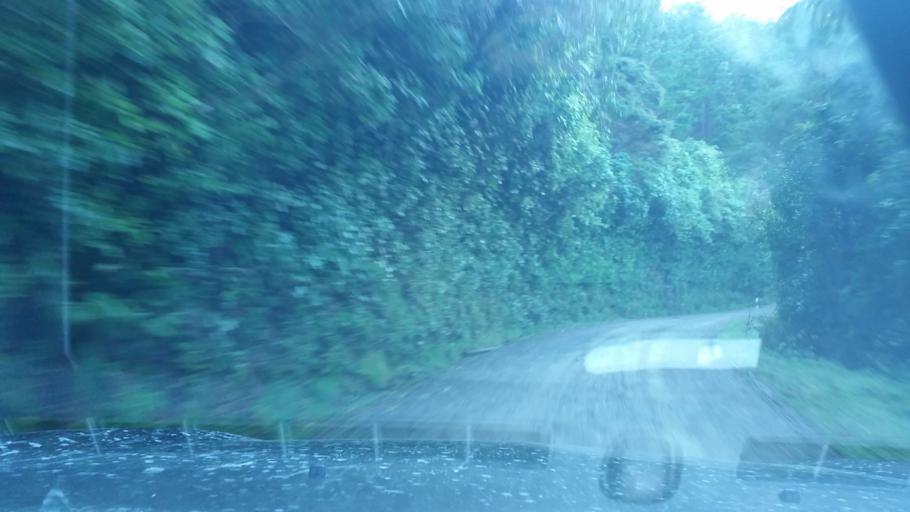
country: NZ
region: Marlborough
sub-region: Marlborough District
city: Picton
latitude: -41.1384
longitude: 174.0527
